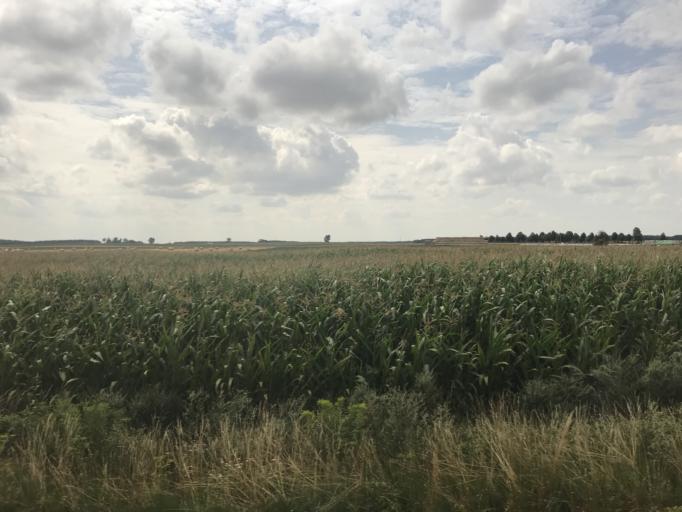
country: PL
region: Greater Poland Voivodeship
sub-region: Powiat gnieznienski
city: Lubowo
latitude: 52.5064
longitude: 17.4882
